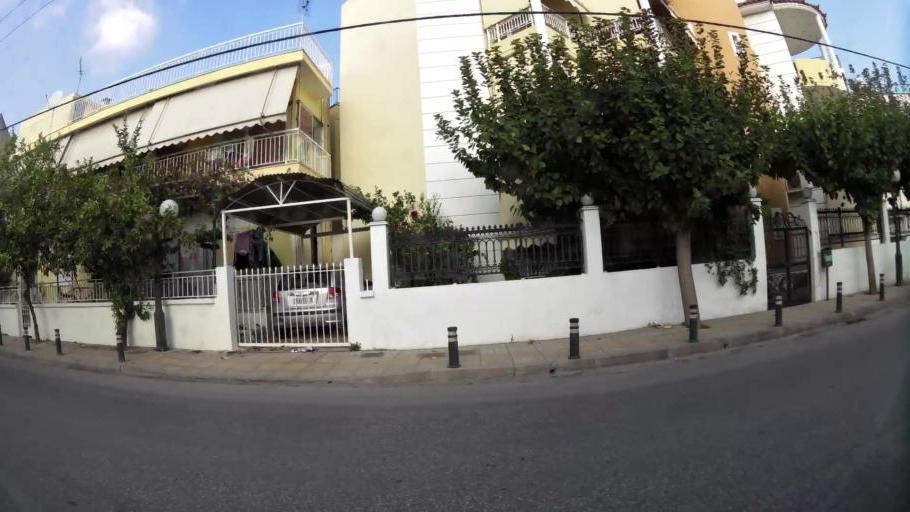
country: GR
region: Attica
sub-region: Nomarchia Anatolikis Attikis
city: Acharnes
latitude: 38.0875
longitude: 23.7447
